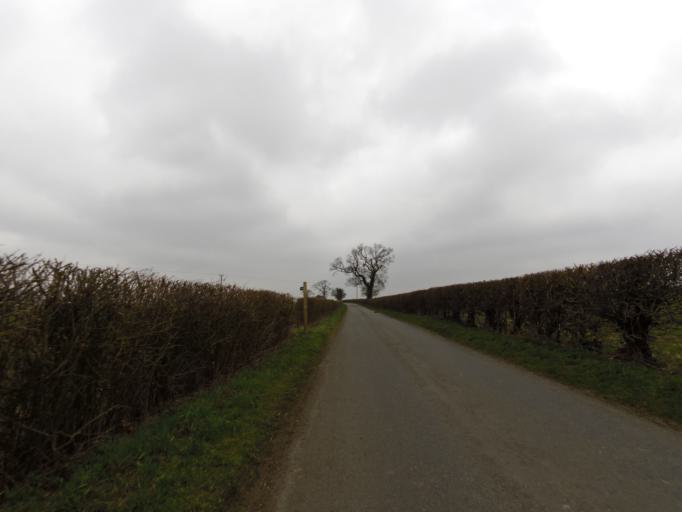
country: GB
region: England
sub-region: Suffolk
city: Framlingham
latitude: 52.2332
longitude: 1.3848
